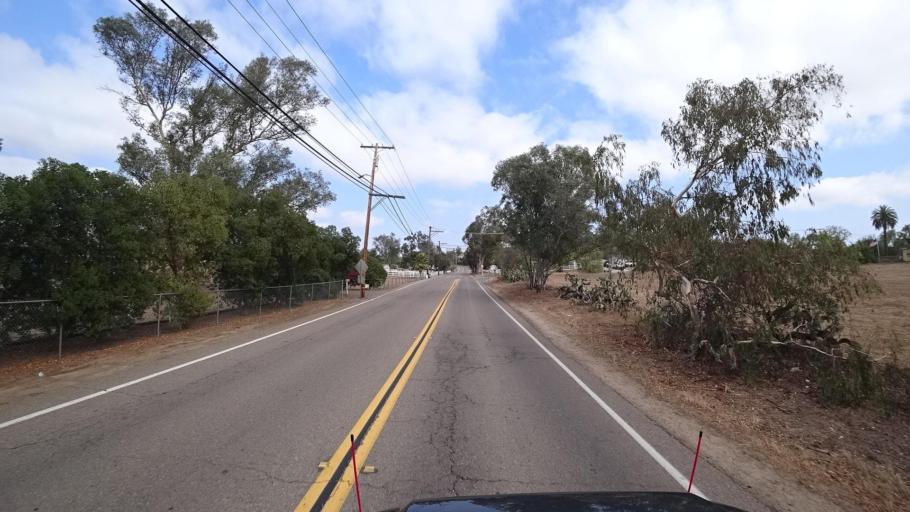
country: US
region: California
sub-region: San Diego County
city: Ramona
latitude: 33.0403
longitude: -116.8503
